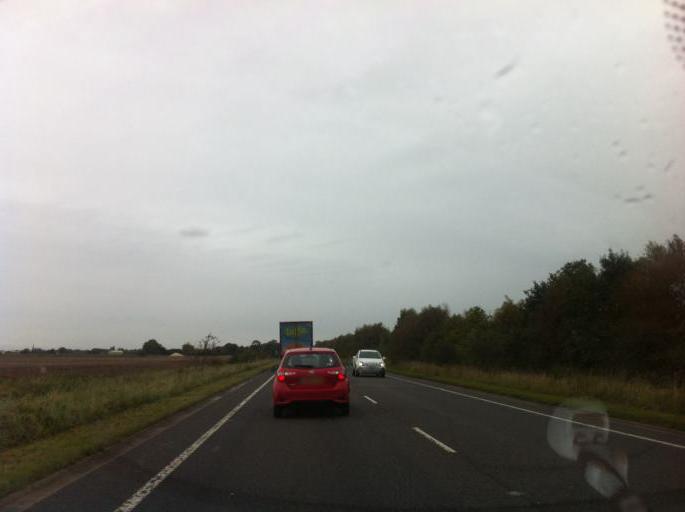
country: GB
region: England
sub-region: Lincolnshire
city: Kirton
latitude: 52.8763
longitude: -0.0950
